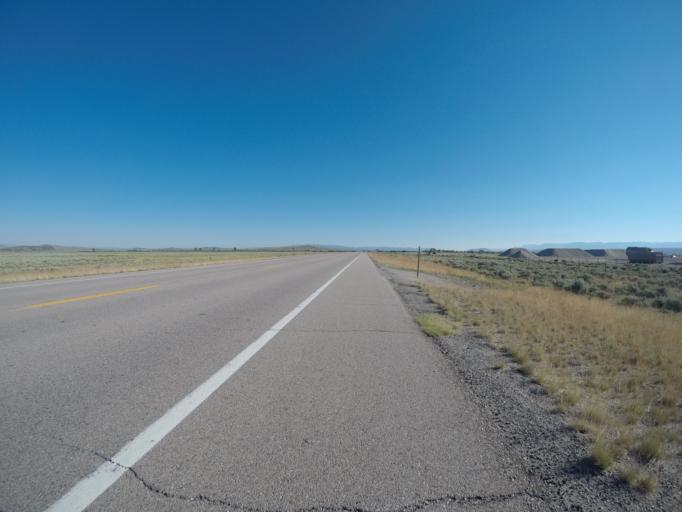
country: US
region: Wyoming
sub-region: Sublette County
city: Pinedale
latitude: 42.9706
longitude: -110.0897
